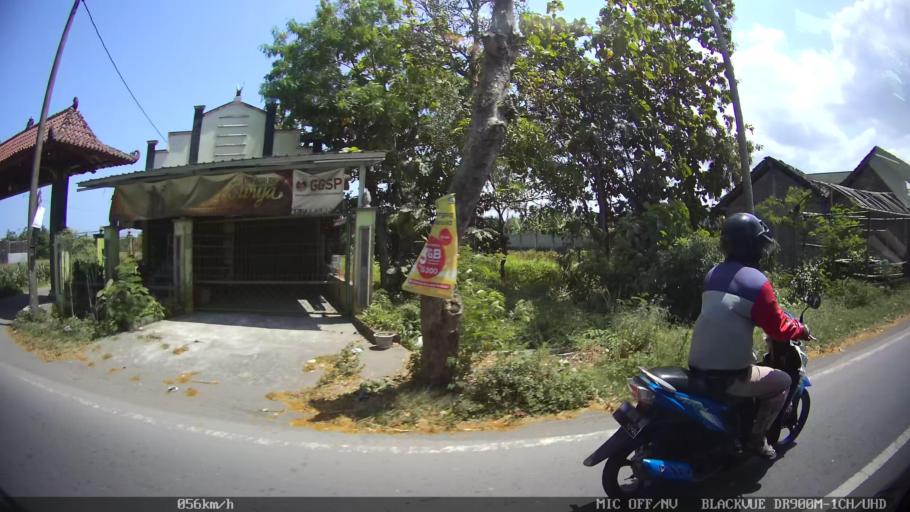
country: ID
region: Daerah Istimewa Yogyakarta
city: Pandak
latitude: -7.9205
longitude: 110.2822
